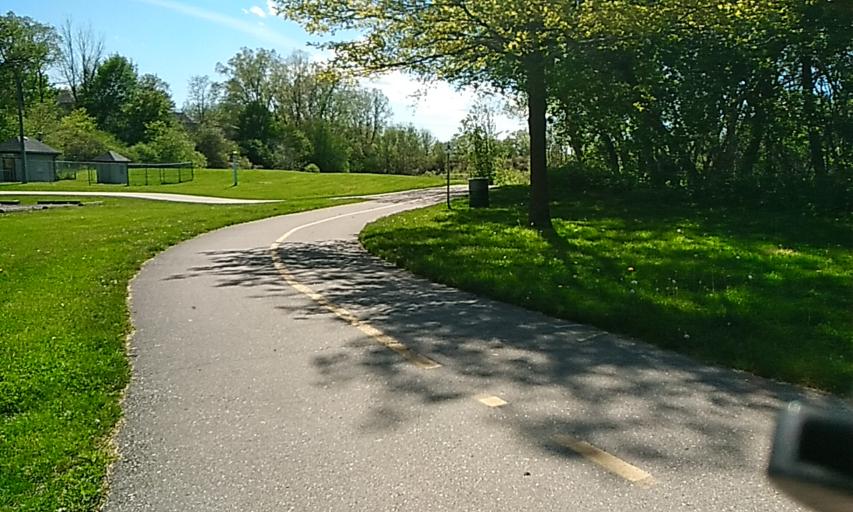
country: CA
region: Ontario
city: London
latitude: 42.9745
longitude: -81.2261
